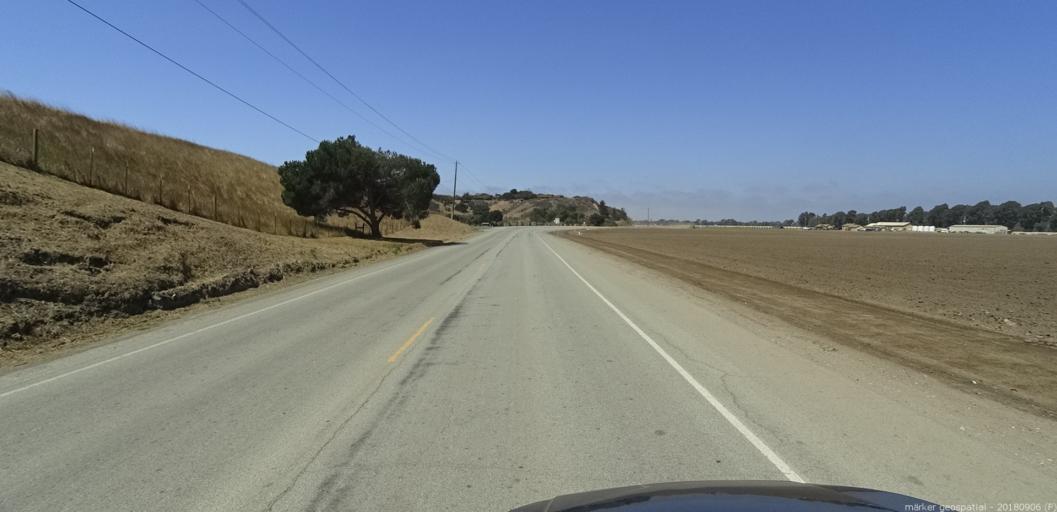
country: US
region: California
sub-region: Monterey County
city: Salinas
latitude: 36.6369
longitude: -121.7017
